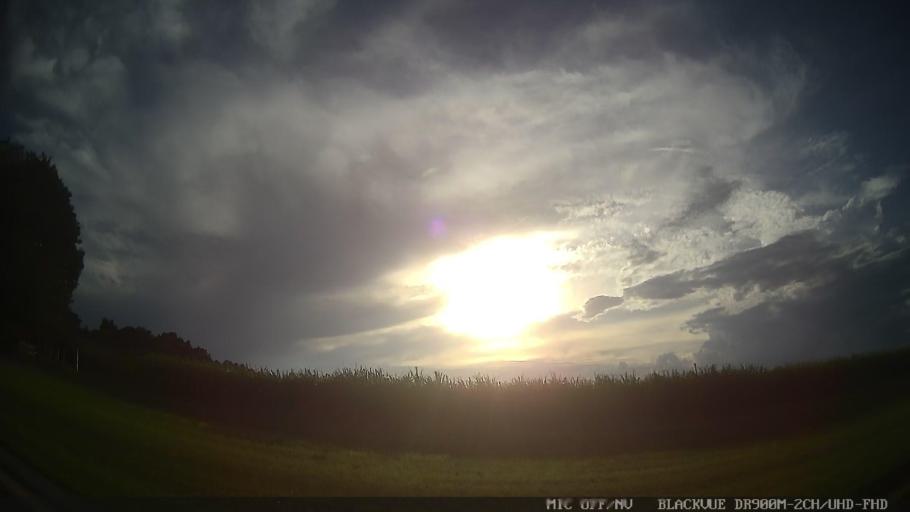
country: BR
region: Sao Paulo
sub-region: Cerquilho
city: Cerquilho
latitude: -23.1747
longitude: -47.6417
